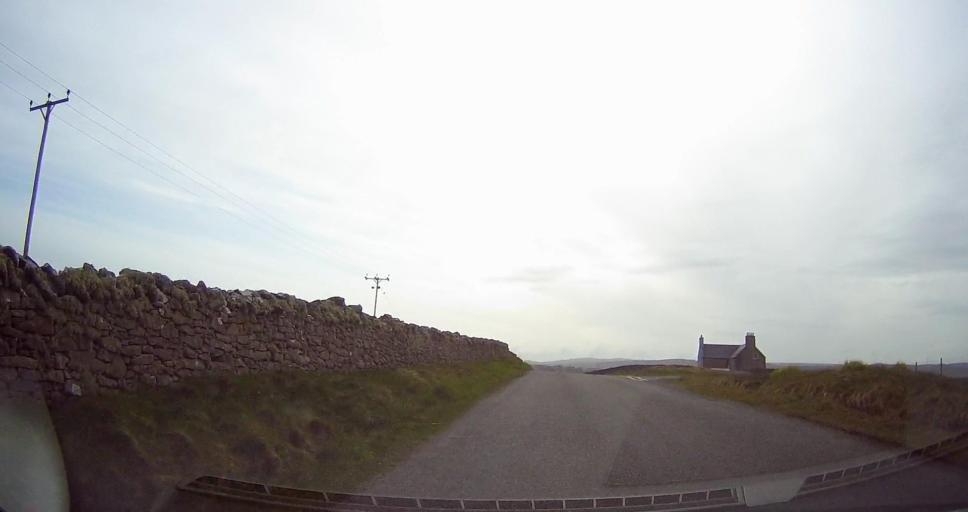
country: GB
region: Scotland
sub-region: Shetland Islands
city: Shetland
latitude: 60.1579
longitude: -1.1180
